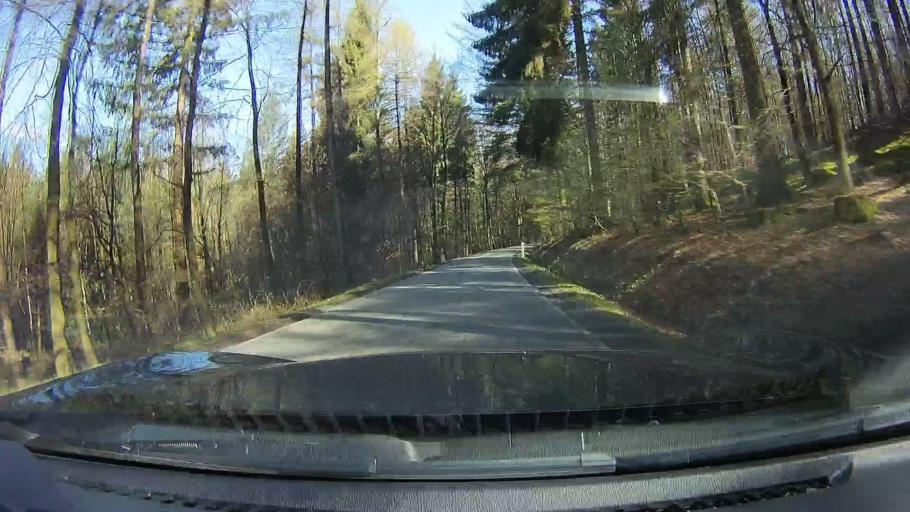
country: DE
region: Baden-Wuerttemberg
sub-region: Karlsruhe Region
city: Neunkirchen
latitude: 49.4117
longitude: 8.9611
